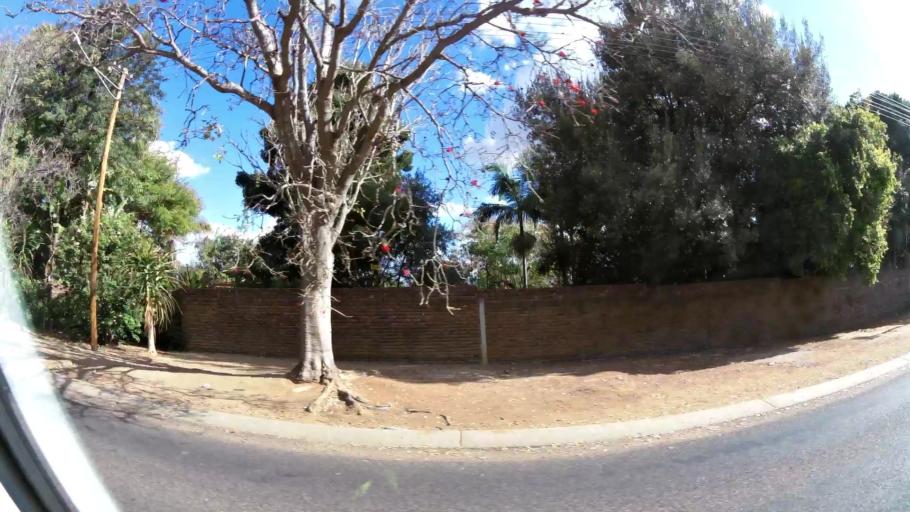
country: ZA
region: Limpopo
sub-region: Capricorn District Municipality
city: Polokwane
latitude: -23.8894
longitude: 29.4690
